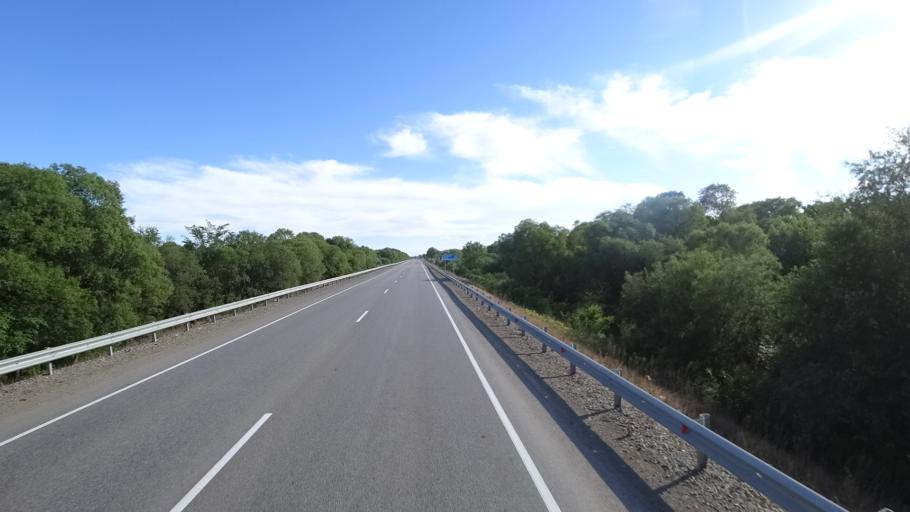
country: RU
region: Khabarovsk Krai
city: Khor
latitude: 47.8800
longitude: 134.9701
